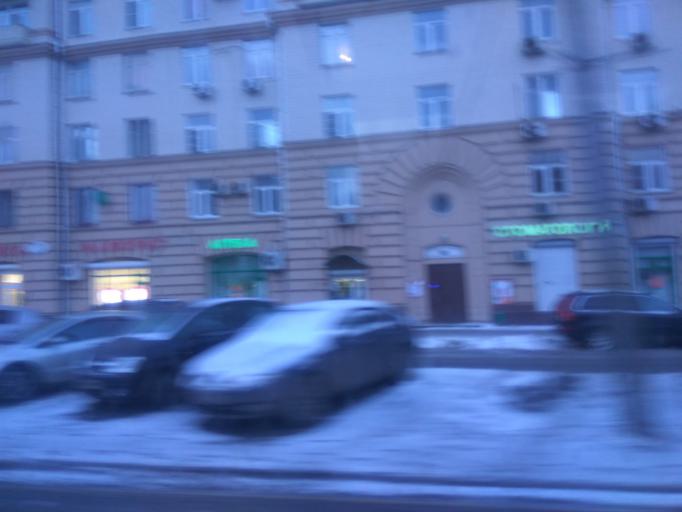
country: RU
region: Moscow
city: Taganskiy
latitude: 55.7285
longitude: 37.6786
